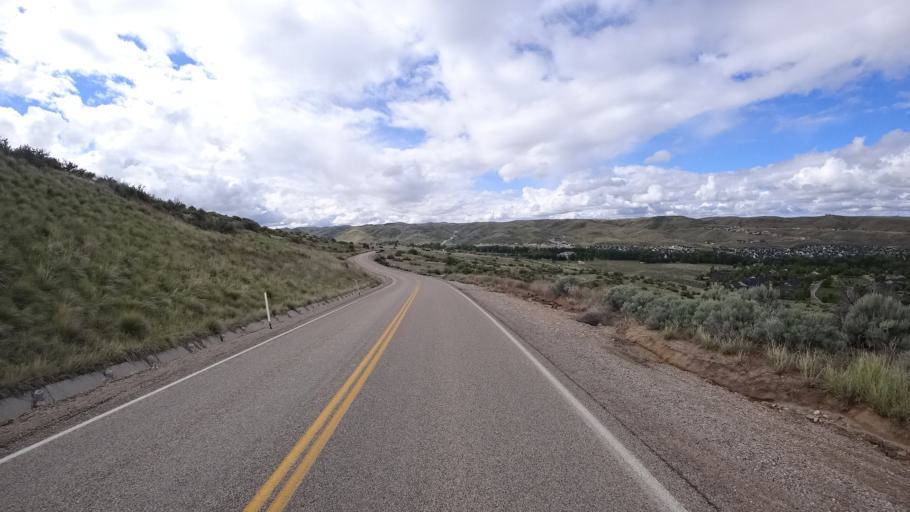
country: US
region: Idaho
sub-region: Ada County
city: Garden City
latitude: 43.7233
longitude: -116.2353
